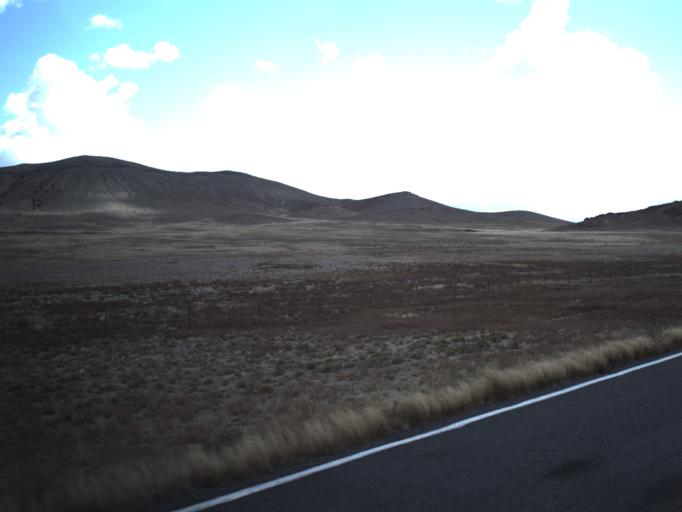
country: US
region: Utah
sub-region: Beaver County
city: Milford
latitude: 38.6369
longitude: -113.8587
